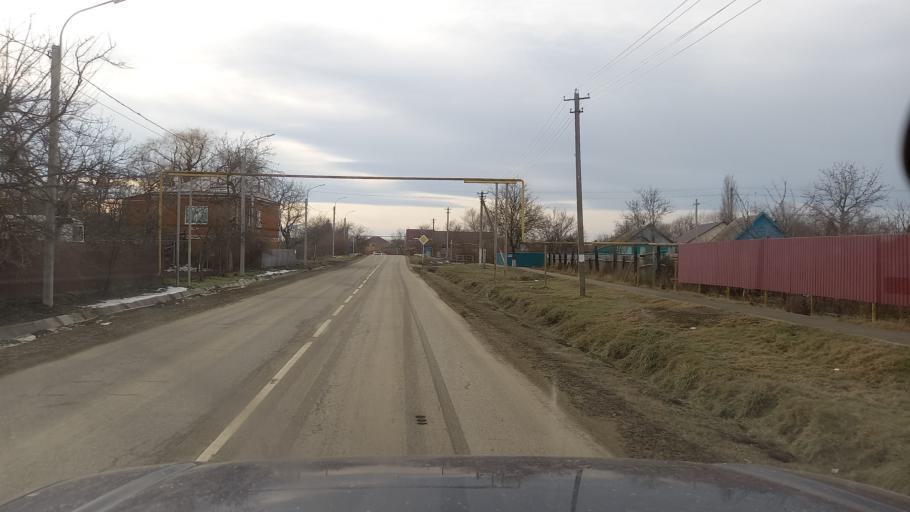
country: RU
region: Krasnodarskiy
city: Belorechensk
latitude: 44.7659
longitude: 39.9011
